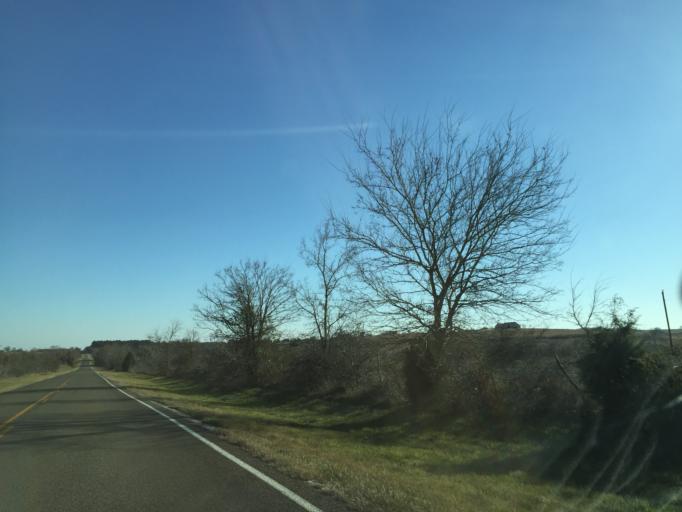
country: US
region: Texas
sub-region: Bastrop County
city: Elgin
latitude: 30.4121
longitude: -97.2544
